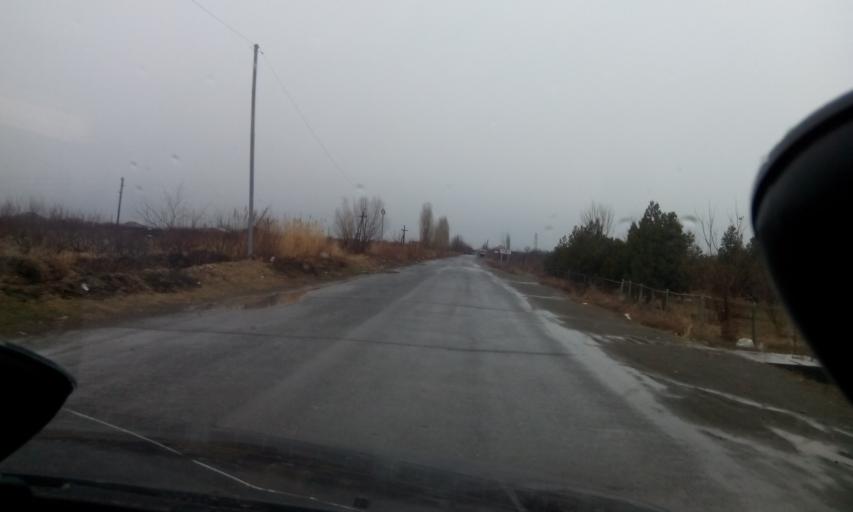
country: AM
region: Armavir
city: Nalbandyan
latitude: 40.0623
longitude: 43.9881
